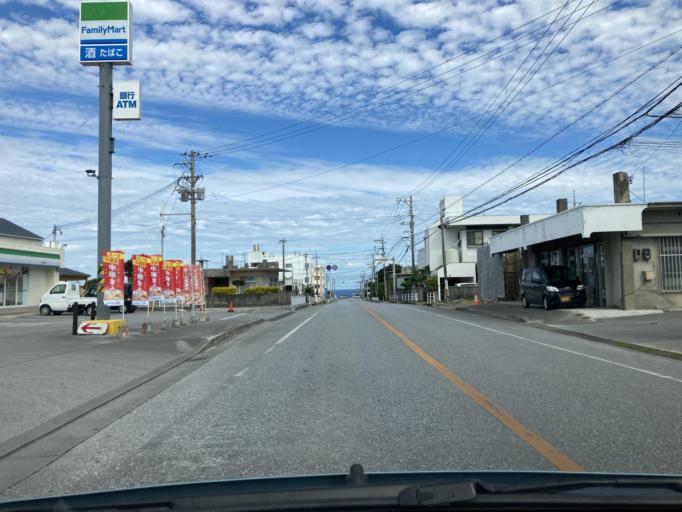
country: JP
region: Okinawa
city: Ishikawa
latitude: 26.4156
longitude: 127.7324
